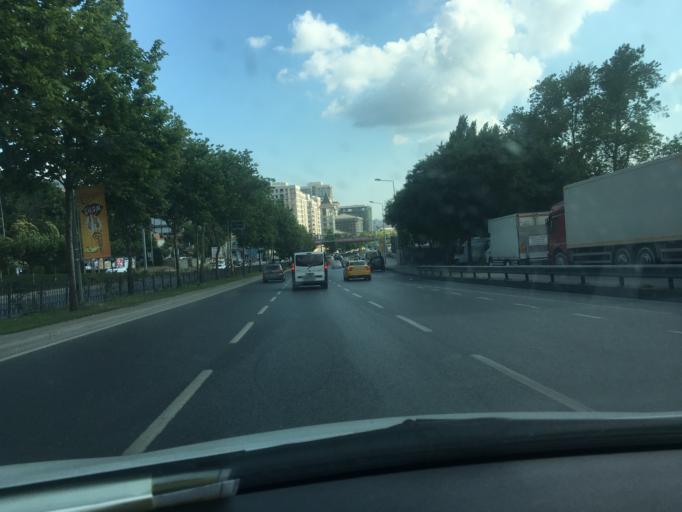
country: TR
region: Istanbul
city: Sisli
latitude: 41.0472
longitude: 28.9680
